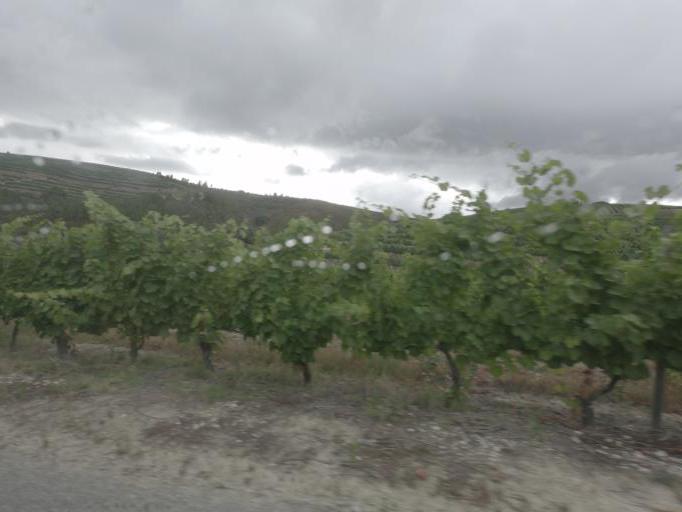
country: PT
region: Vila Real
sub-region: Sabrosa
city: Sabrosa
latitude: 41.2397
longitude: -7.4945
